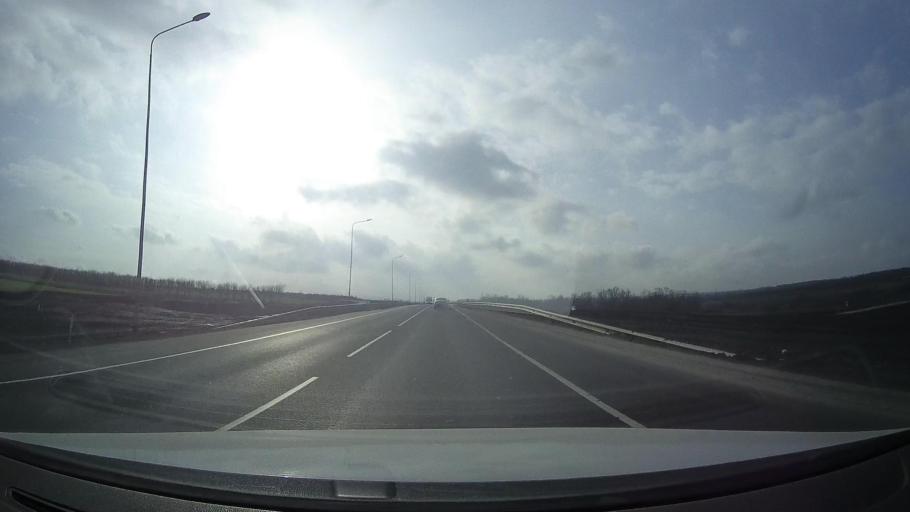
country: RU
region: Rostov
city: Grushevskaya
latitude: 47.4287
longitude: 39.8666
